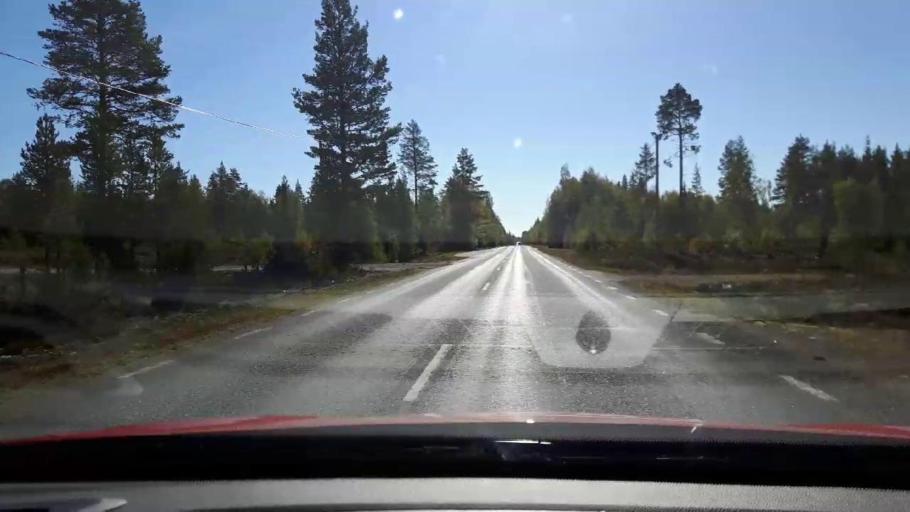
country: SE
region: Jaemtland
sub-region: Harjedalens Kommun
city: Sveg
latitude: 62.4072
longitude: 13.9248
